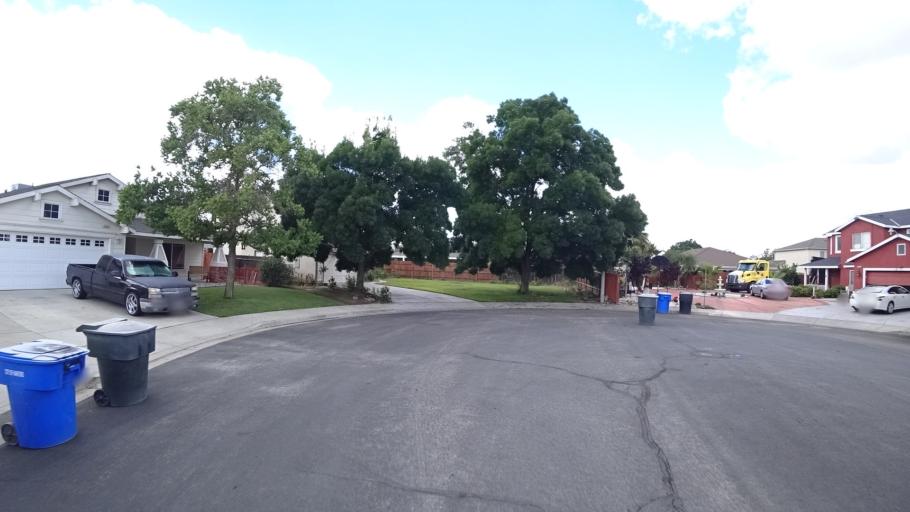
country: US
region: California
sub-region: Kings County
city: Hanford
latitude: 36.3438
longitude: -119.6267
